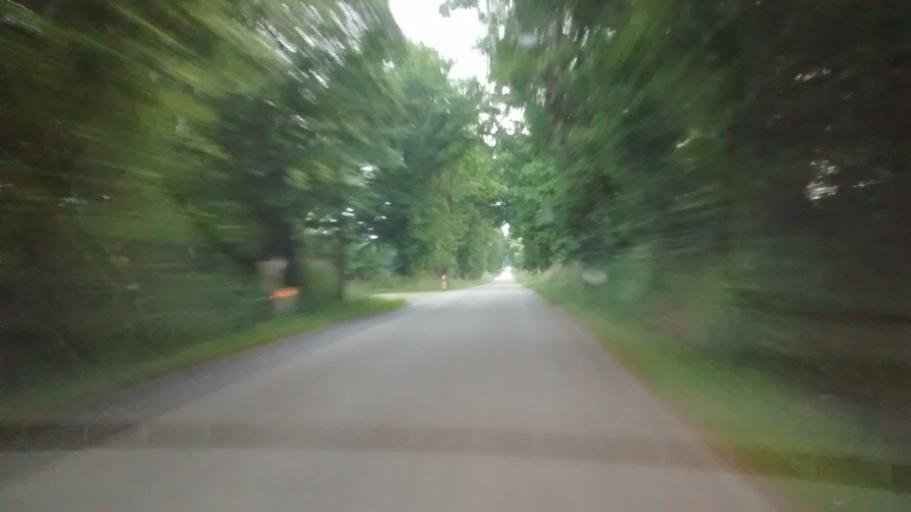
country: FR
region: Brittany
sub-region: Departement du Morbihan
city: Pleucadeuc
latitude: 47.7354
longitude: -2.3398
